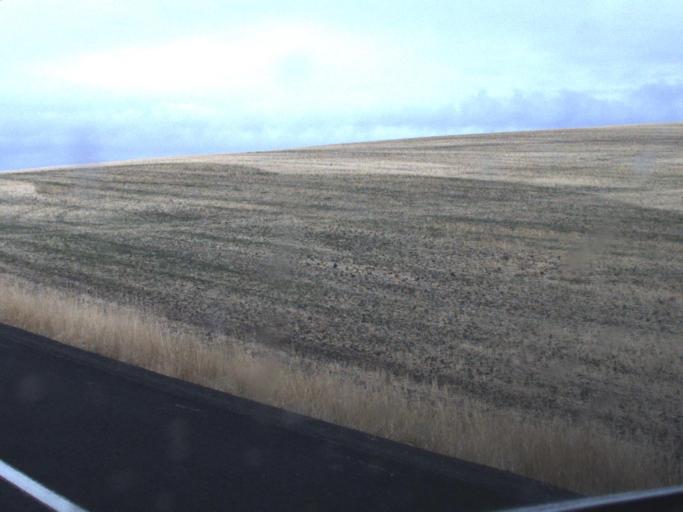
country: US
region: Washington
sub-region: Whitman County
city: Pullman
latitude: 46.5857
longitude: -117.1612
